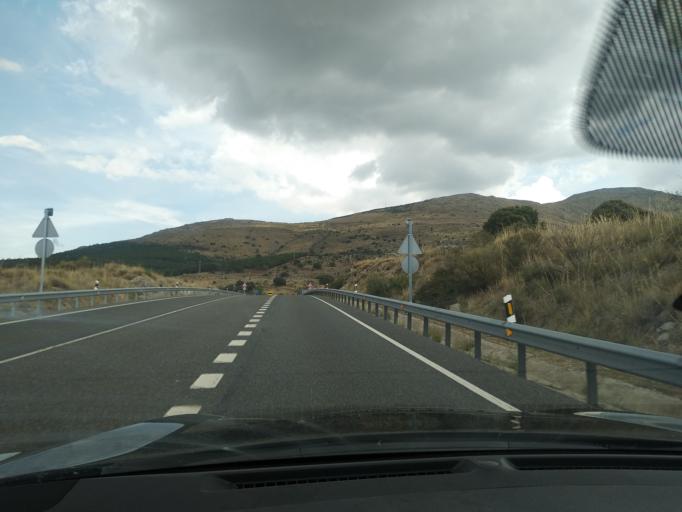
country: ES
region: Castille and Leon
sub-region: Provincia de Segovia
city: Otero de Herreros
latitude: 40.7681
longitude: -4.2023
